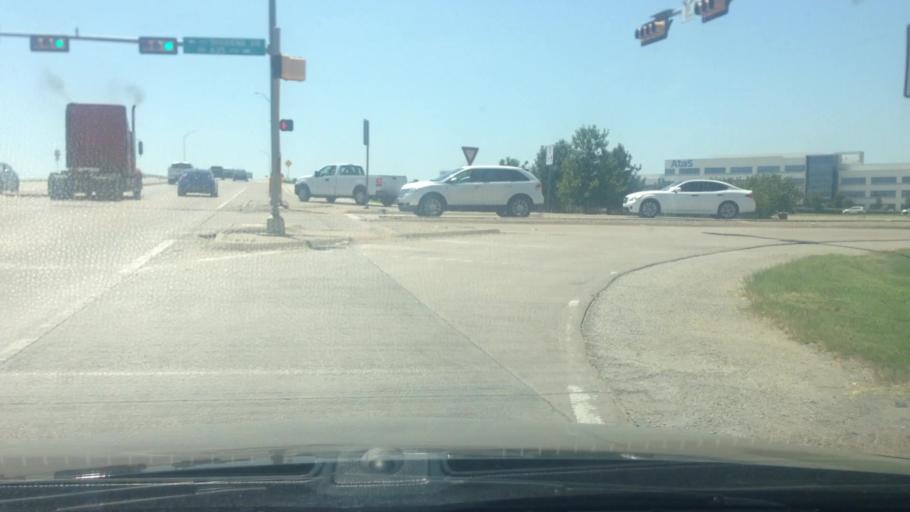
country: US
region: Texas
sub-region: Dallas County
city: Coppell
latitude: 32.9374
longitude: -97.0078
